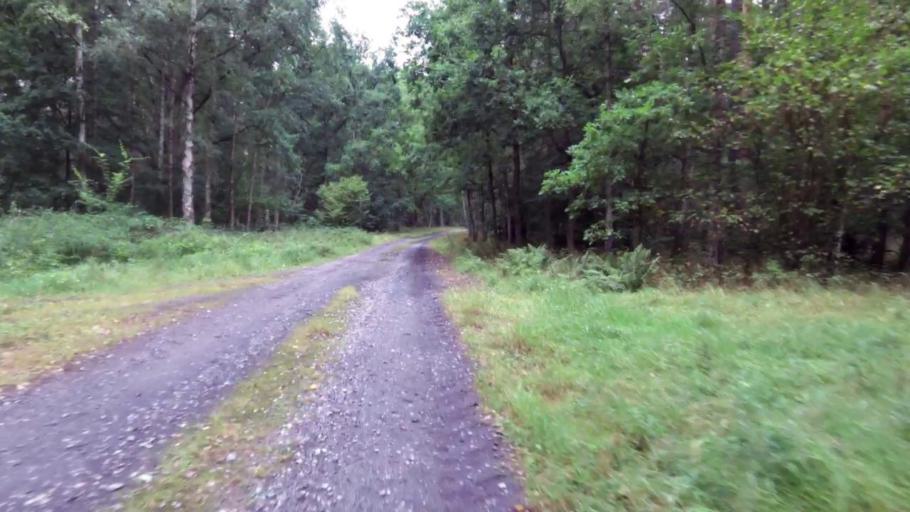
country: PL
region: West Pomeranian Voivodeship
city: Trzcinsko Zdroj
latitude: 52.8752
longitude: 14.6853
